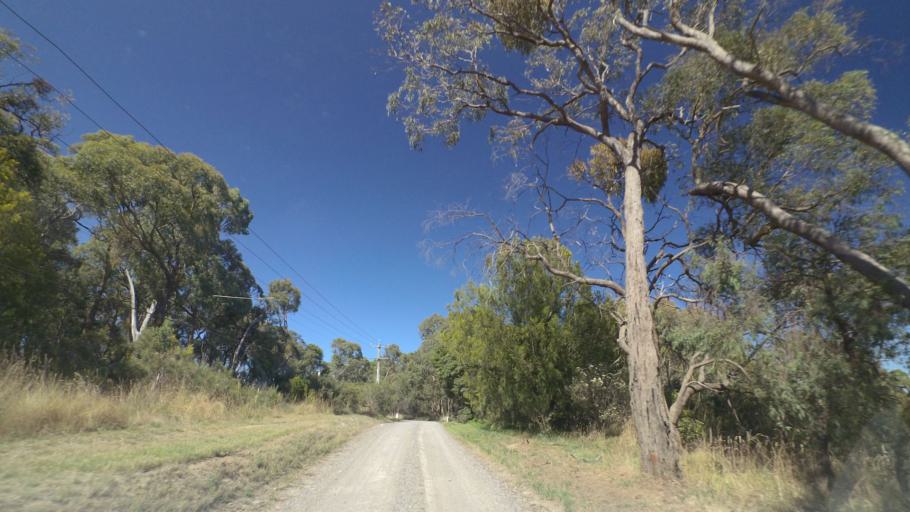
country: AU
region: Victoria
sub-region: Knox
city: Wantirna South
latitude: -37.8696
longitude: 145.2005
